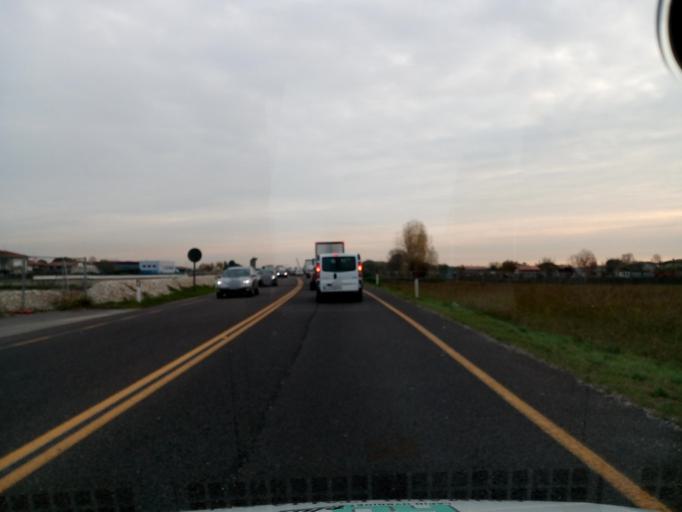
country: IT
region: Veneto
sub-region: Provincia di Vicenza
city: San Zeno-San Giuseppe
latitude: 45.7380
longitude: 11.7679
